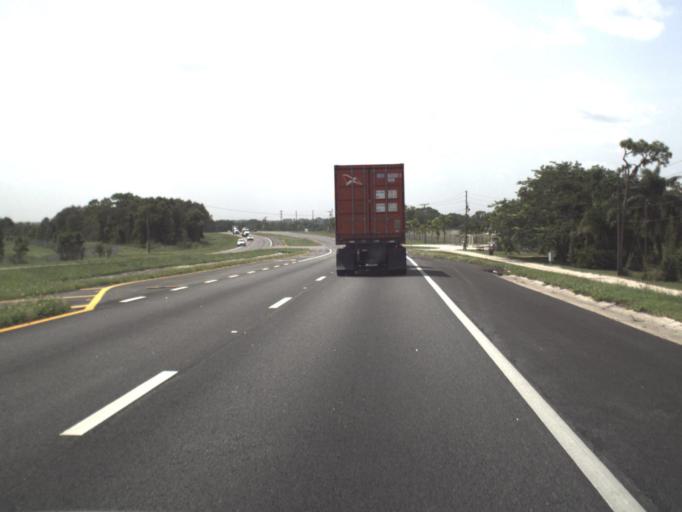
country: US
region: Florida
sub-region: Polk County
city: Frostproof
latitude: 27.7055
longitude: -81.5636
